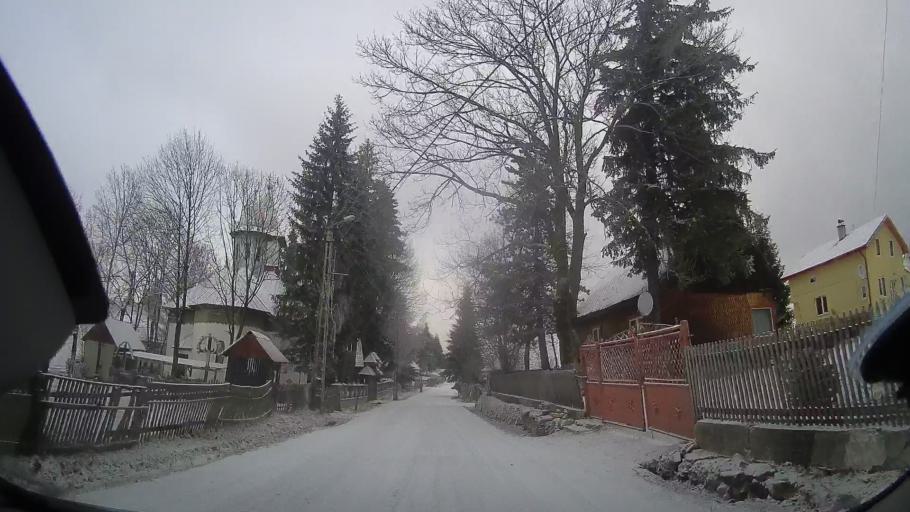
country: RO
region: Cluj
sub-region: Comuna Marisel
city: Marisel
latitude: 46.6612
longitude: 23.1293
